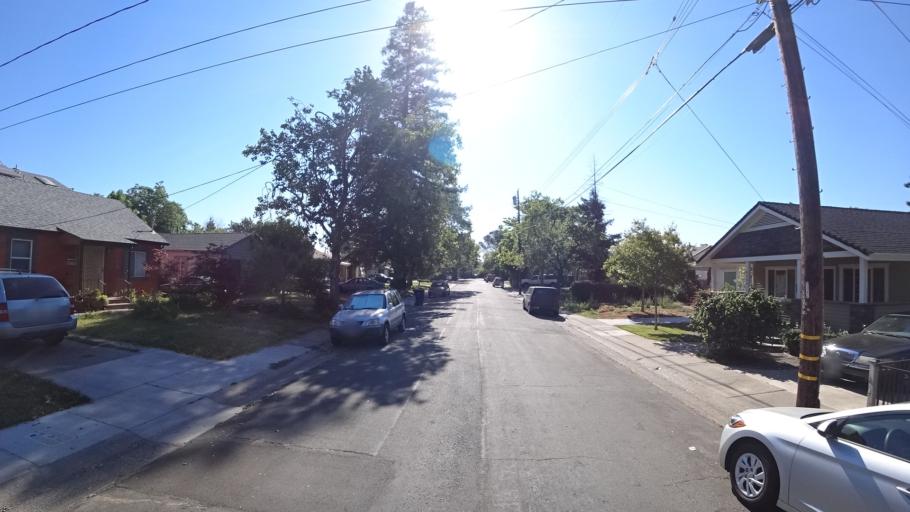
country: US
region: California
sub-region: Sacramento County
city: Parkway
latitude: 38.5435
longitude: -121.4428
